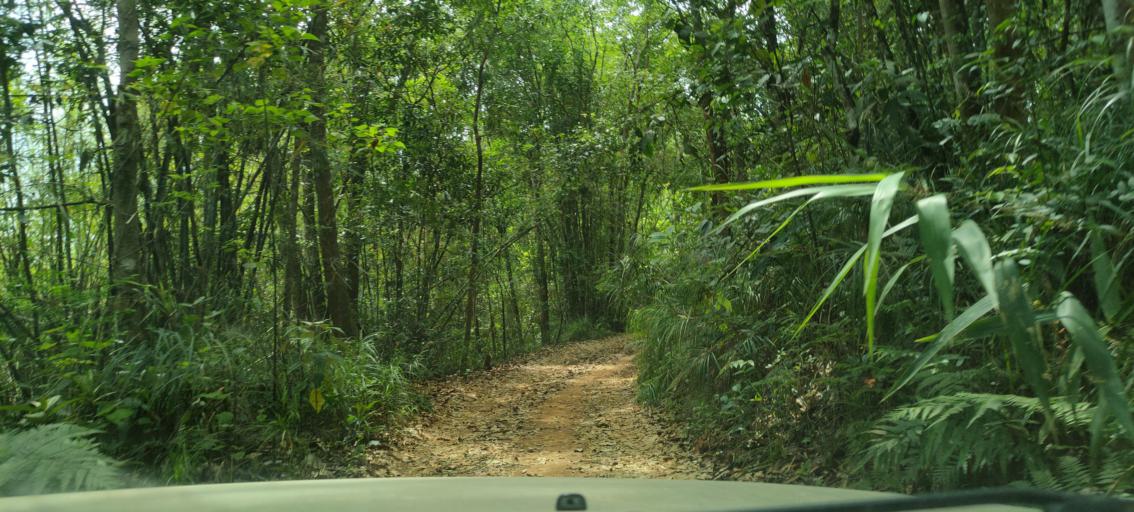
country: LA
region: Loungnamtha
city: Muang Nale
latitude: 20.4140
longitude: 101.4792
